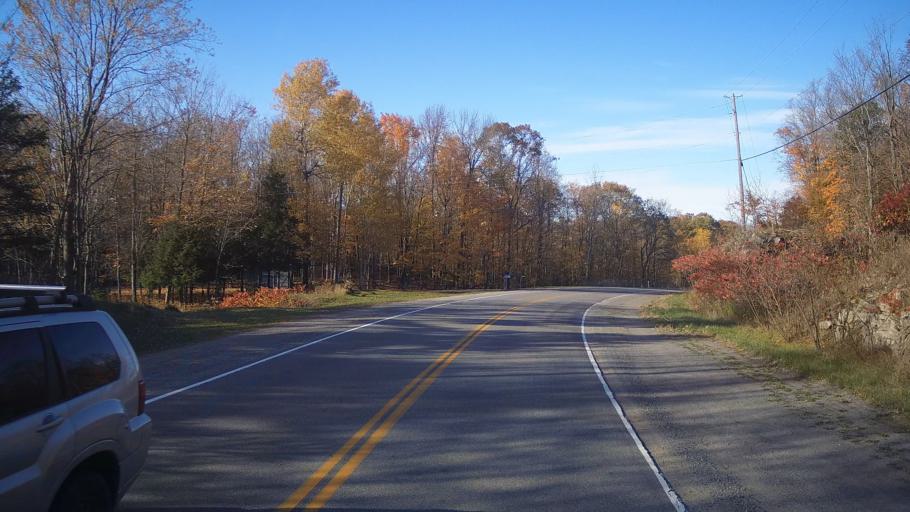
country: CA
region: Ontario
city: Kingston
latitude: 44.4932
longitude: -76.4779
